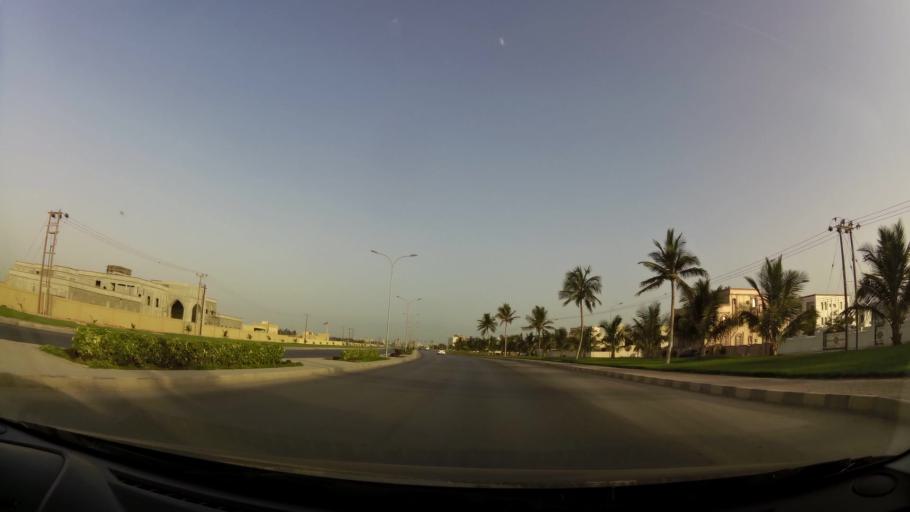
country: OM
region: Zufar
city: Salalah
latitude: 17.0155
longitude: 54.0357
